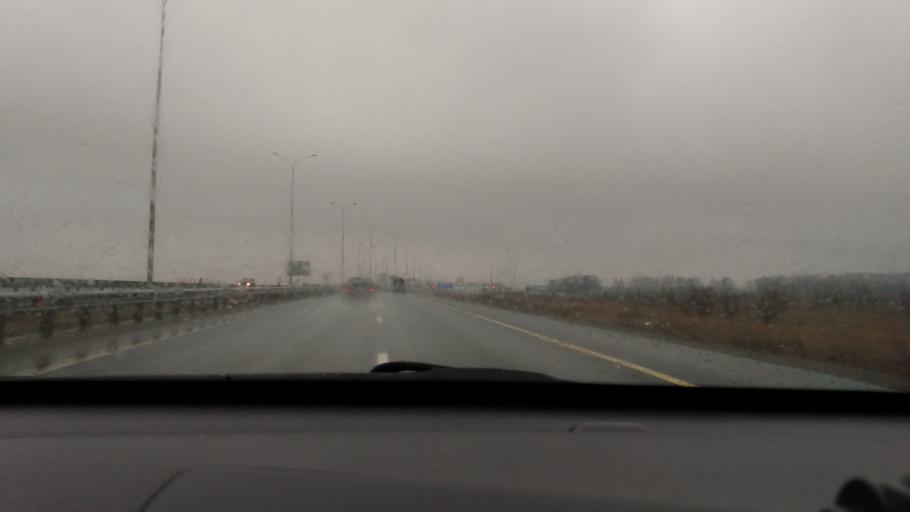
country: RU
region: Moskovskaya
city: Ozherel'ye
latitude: 54.6998
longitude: 38.1625
